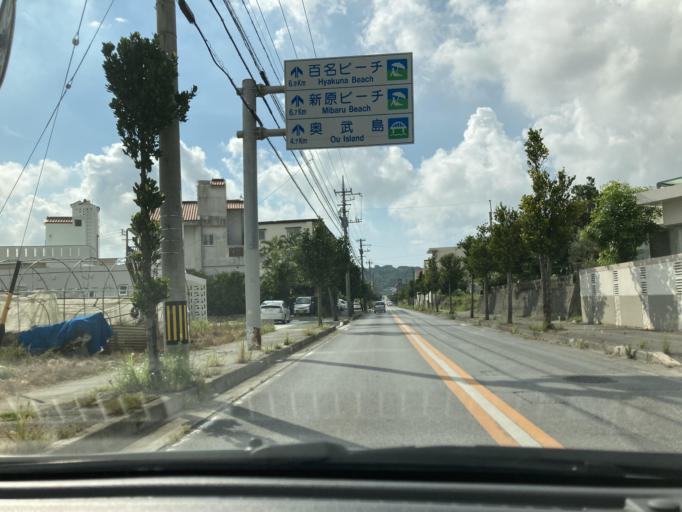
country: JP
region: Okinawa
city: Tomigusuku
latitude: 26.1576
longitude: 127.7483
